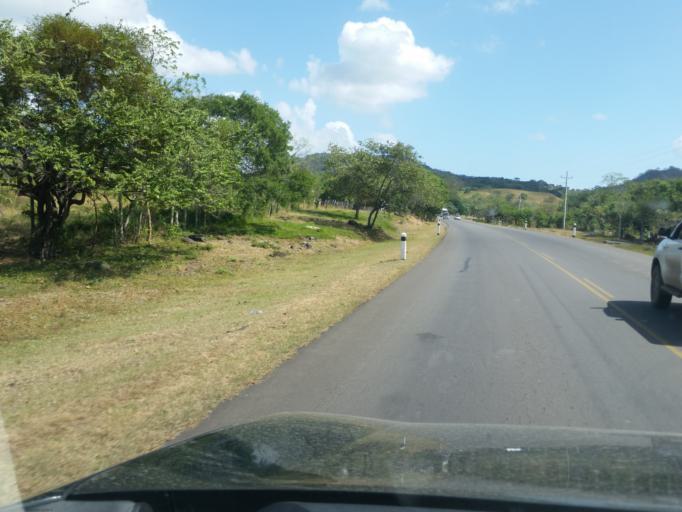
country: NI
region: Chontales
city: Comalapa
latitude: 12.1910
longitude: -85.6102
